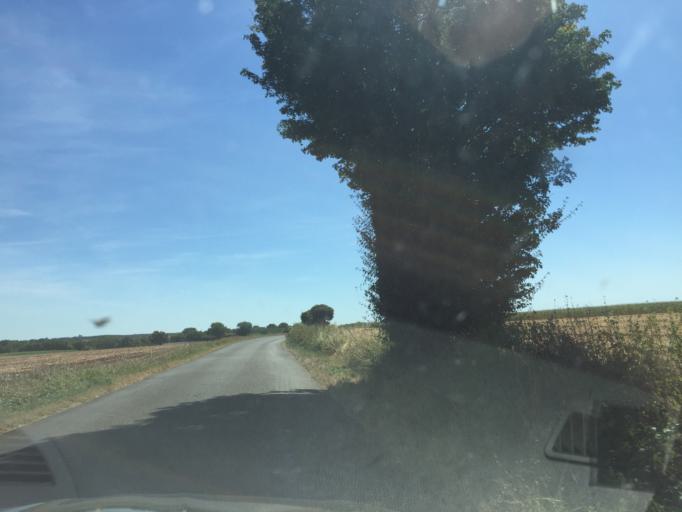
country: FR
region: Poitou-Charentes
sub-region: Departement de la Vienne
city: Vivonne
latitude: 46.4393
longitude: 0.2944
